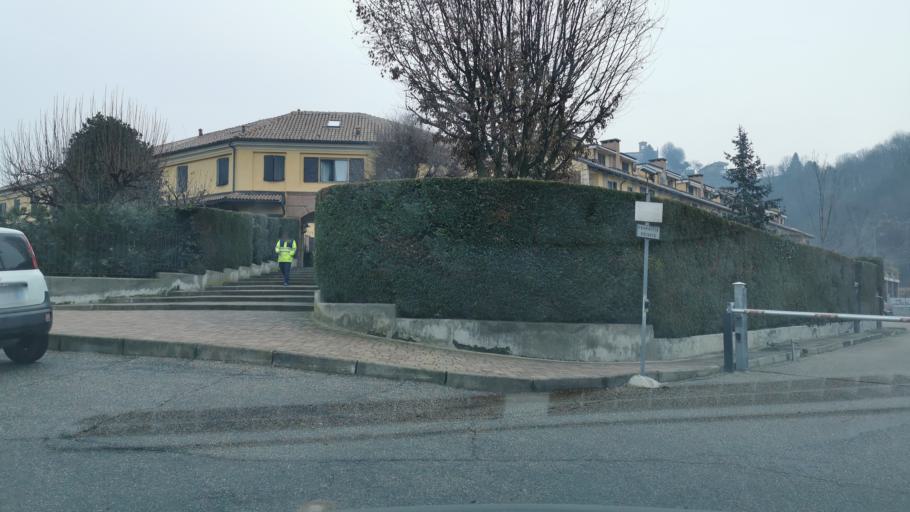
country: IT
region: Piedmont
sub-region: Provincia di Torino
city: Castiglione Torinese
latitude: 45.1181
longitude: 7.8064
